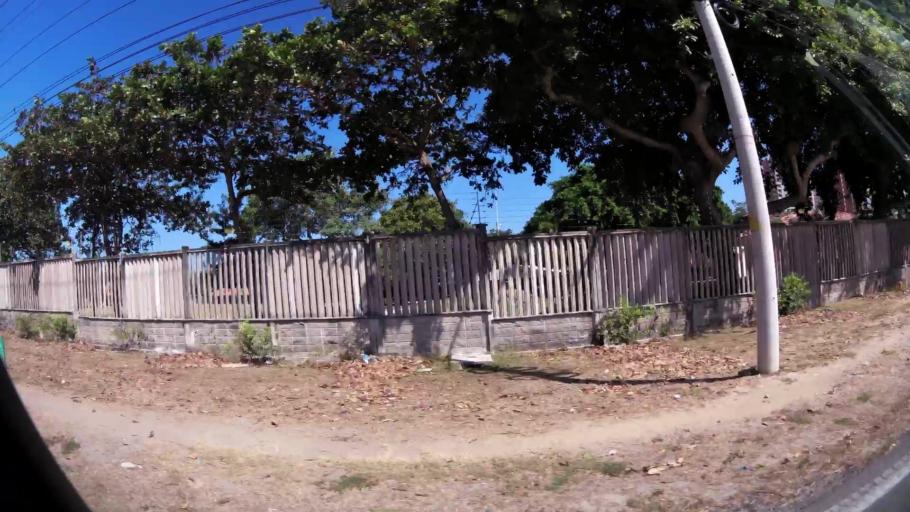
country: CO
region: Atlantico
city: Barranquilla
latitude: 11.0166
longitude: -74.8430
